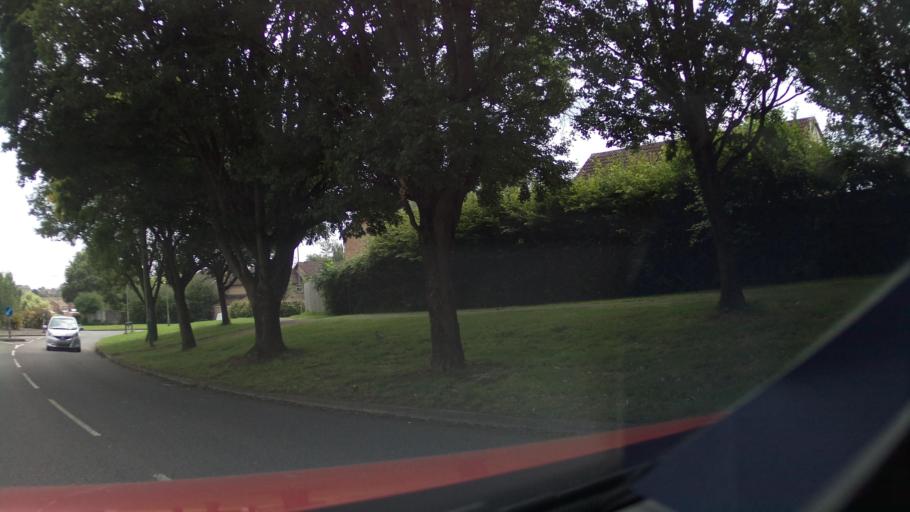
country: GB
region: England
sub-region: Wiltshire
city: Lydiard Tregoze
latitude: 51.5572
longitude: -1.8404
